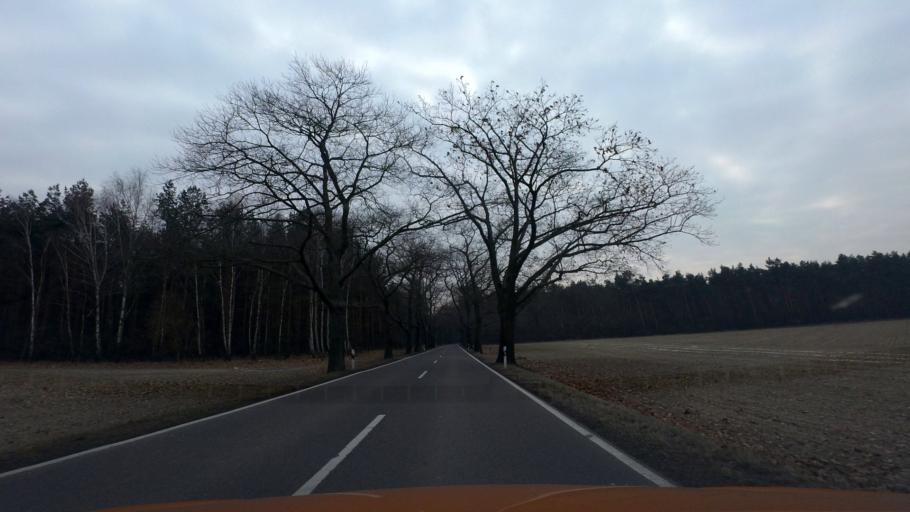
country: DE
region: Brandenburg
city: Ludwigsfelde
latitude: 52.2730
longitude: 13.2189
